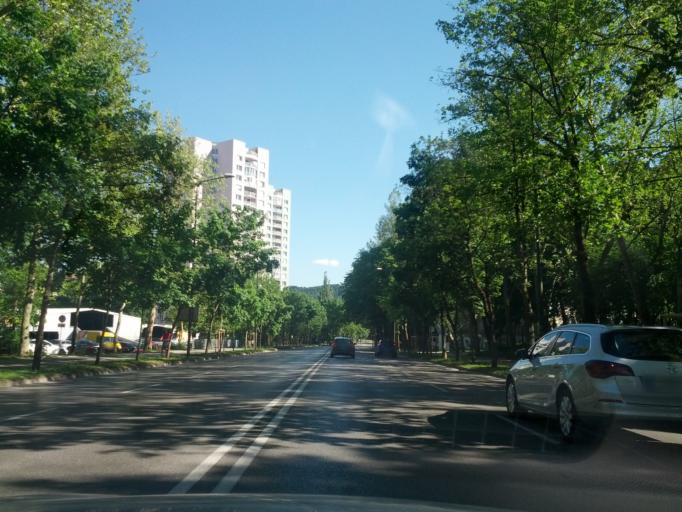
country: SI
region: Ljubljana
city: Ljubljana
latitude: 46.0625
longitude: 14.5194
